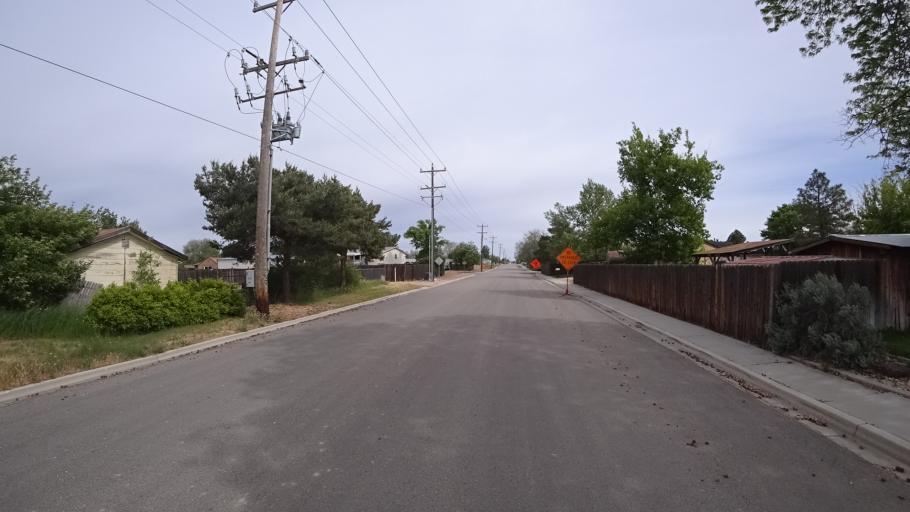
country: US
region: Idaho
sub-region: Ada County
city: Kuna
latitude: 43.5283
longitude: -116.3145
